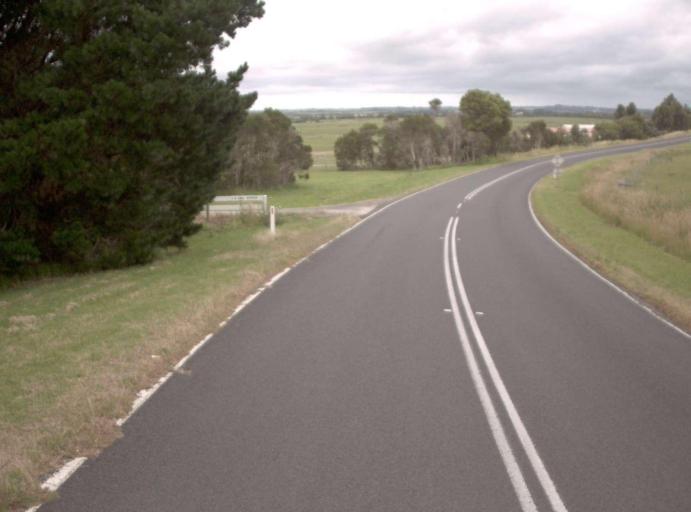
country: AU
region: Victoria
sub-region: Bass Coast
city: North Wonthaggi
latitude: -38.5537
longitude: 145.6545
